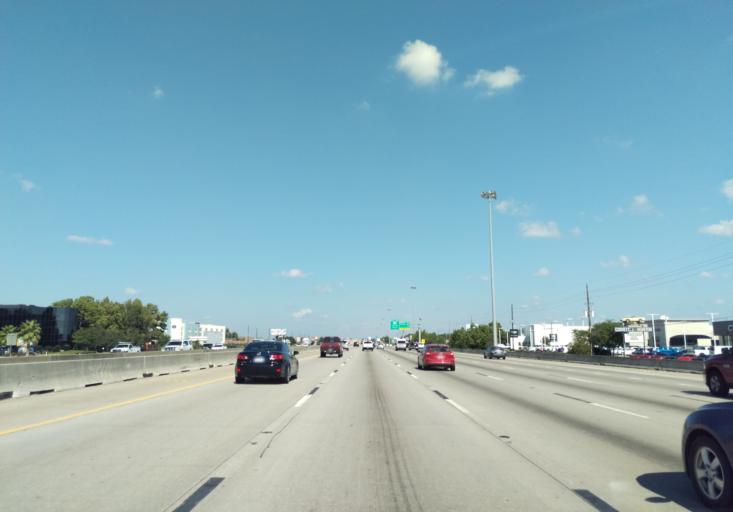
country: US
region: Texas
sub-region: Harris County
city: Aldine
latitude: 29.9902
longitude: -95.4241
